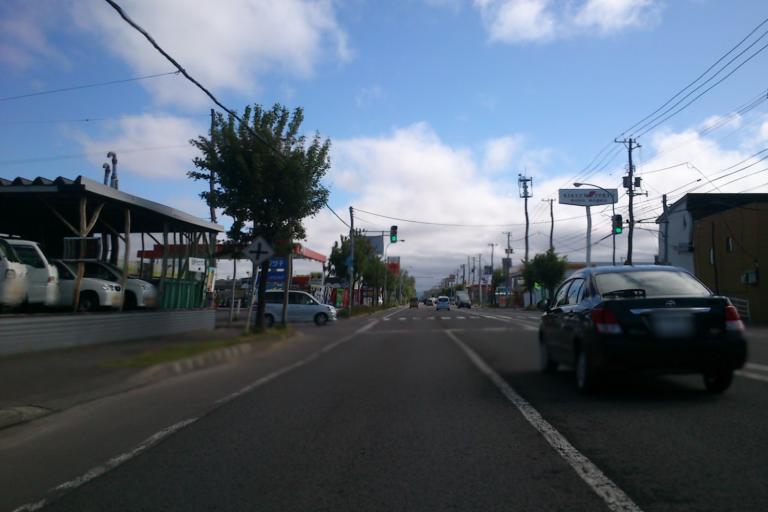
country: JP
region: Hokkaido
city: Sapporo
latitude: 43.1458
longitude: 141.2799
